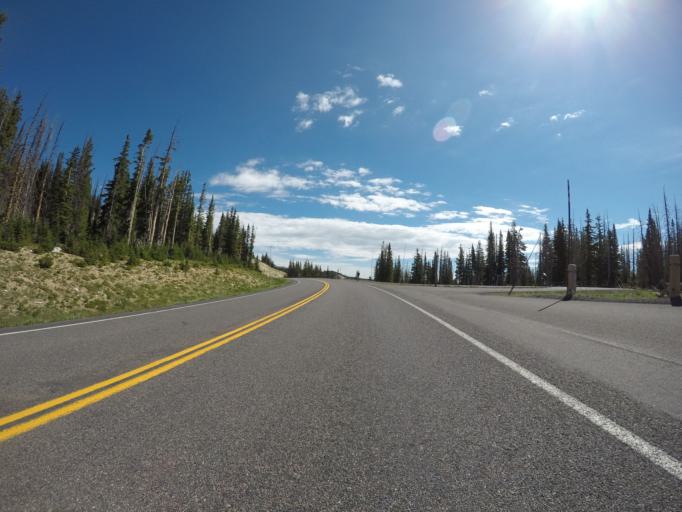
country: US
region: Wyoming
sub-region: Carbon County
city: Saratoga
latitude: 41.3142
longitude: -106.3509
